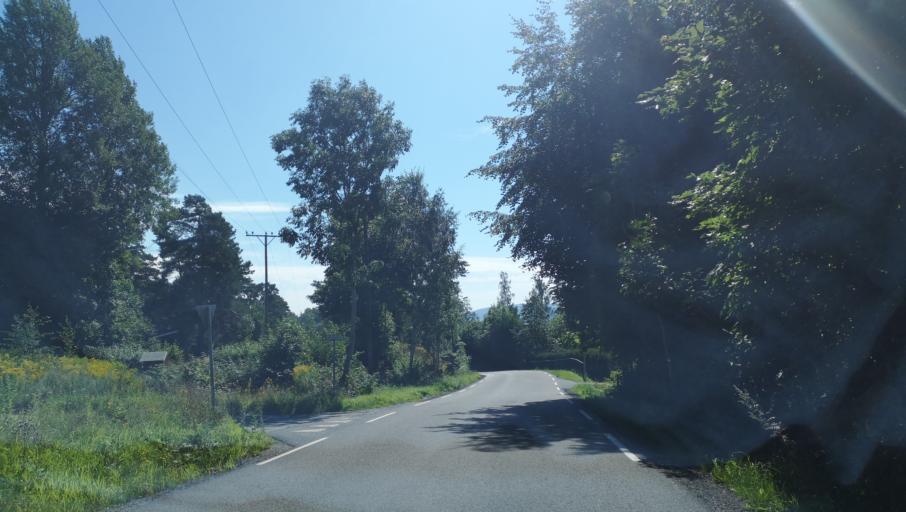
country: NO
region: Akershus
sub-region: Vestby
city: Vestby
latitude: 59.5345
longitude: 10.6893
